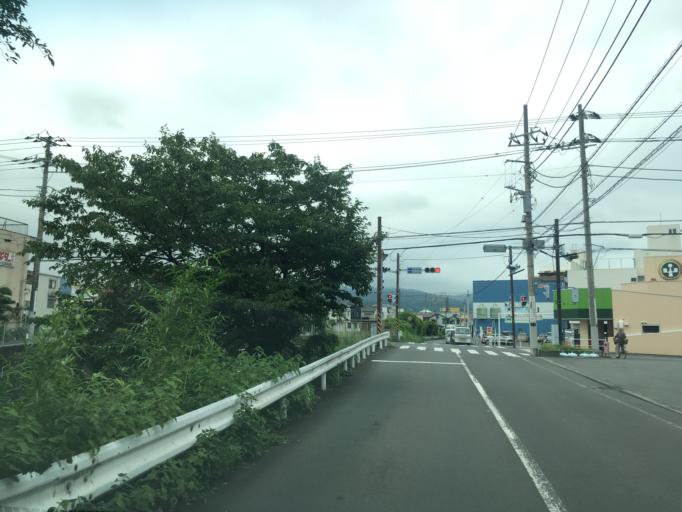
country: JP
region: Kanagawa
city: Odawara
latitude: 35.2617
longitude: 139.1635
